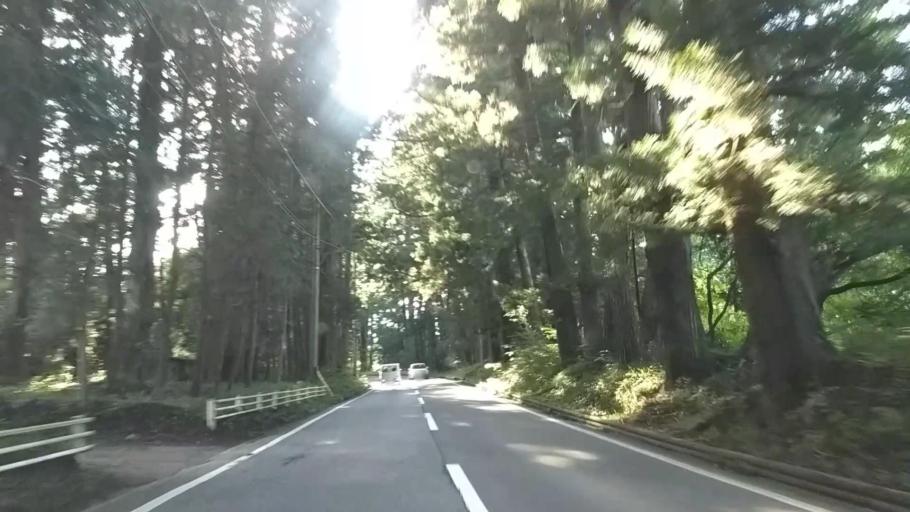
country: JP
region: Tochigi
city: Imaichi
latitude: 36.7380
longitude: 139.6991
